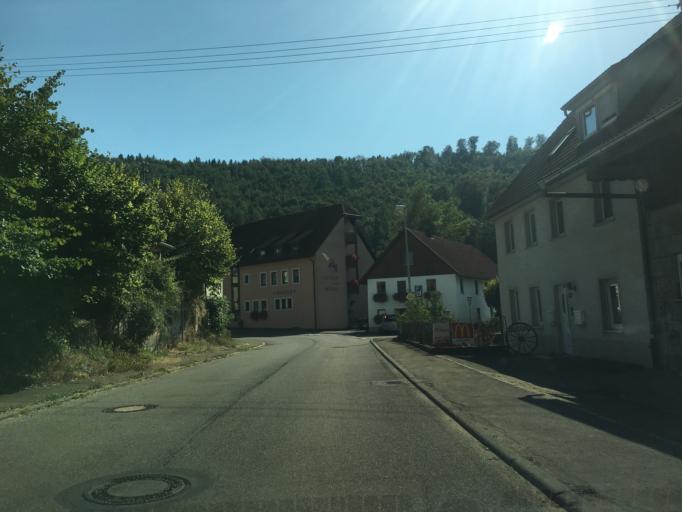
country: DE
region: Baden-Wuerttemberg
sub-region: Tuebingen Region
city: Munsingen
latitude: 48.3433
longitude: 9.4880
